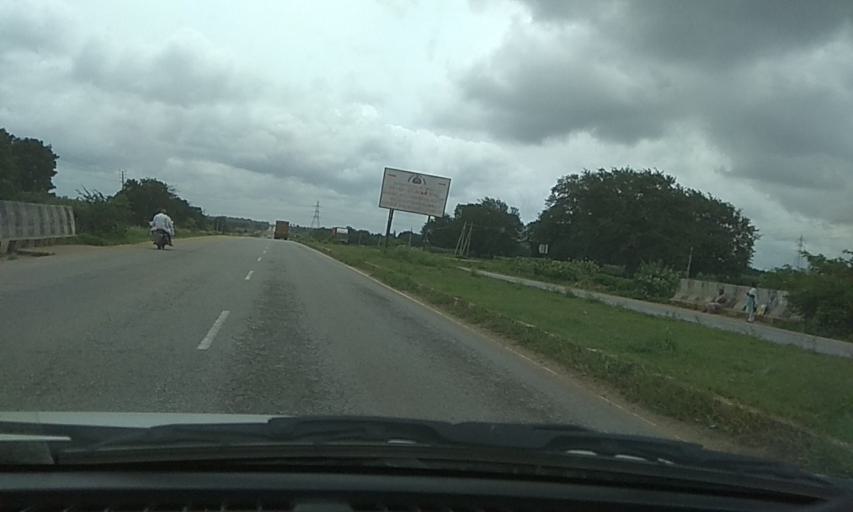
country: IN
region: Karnataka
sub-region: Davanagere
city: Mayakonda
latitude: 14.3707
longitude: 76.1284
